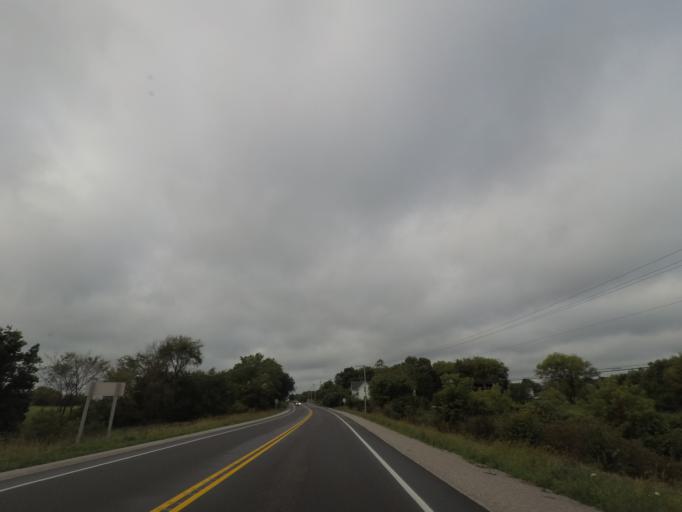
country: US
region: Wisconsin
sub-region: Jefferson County
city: Jefferson
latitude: 43.0091
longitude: -88.7695
